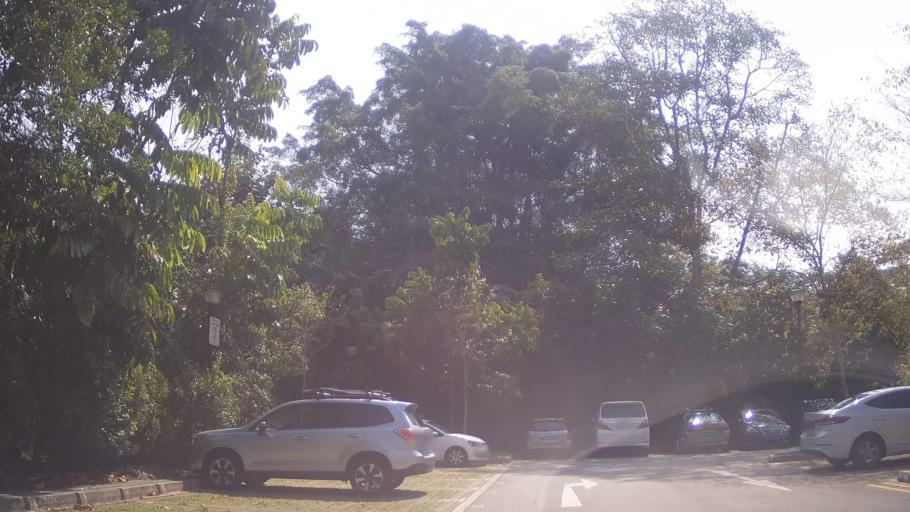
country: MY
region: Johor
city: Johor Bahru
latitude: 1.3720
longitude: 103.7798
